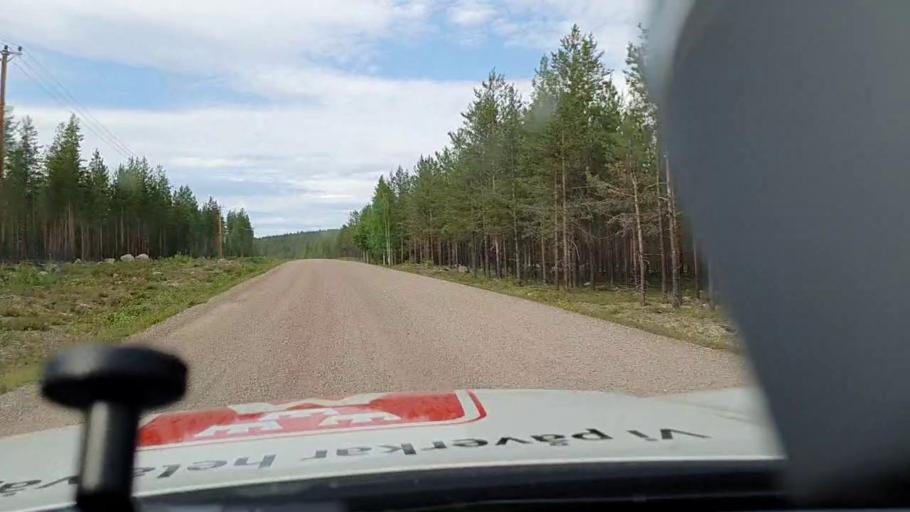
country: SE
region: Norrbotten
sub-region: Alvsbyns Kommun
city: AElvsbyn
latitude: 66.1233
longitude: 20.9936
